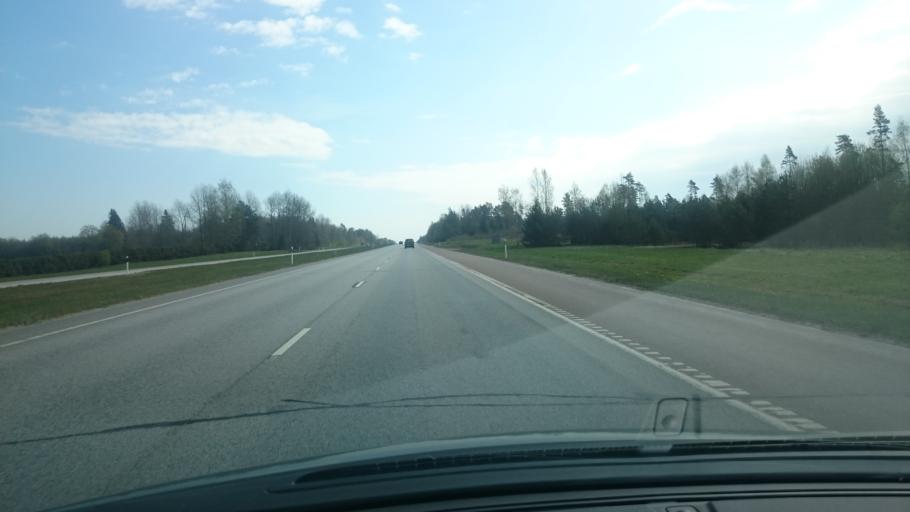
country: EE
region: Harju
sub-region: Raasiku vald
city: Raasiku
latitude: 59.4356
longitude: 25.2080
